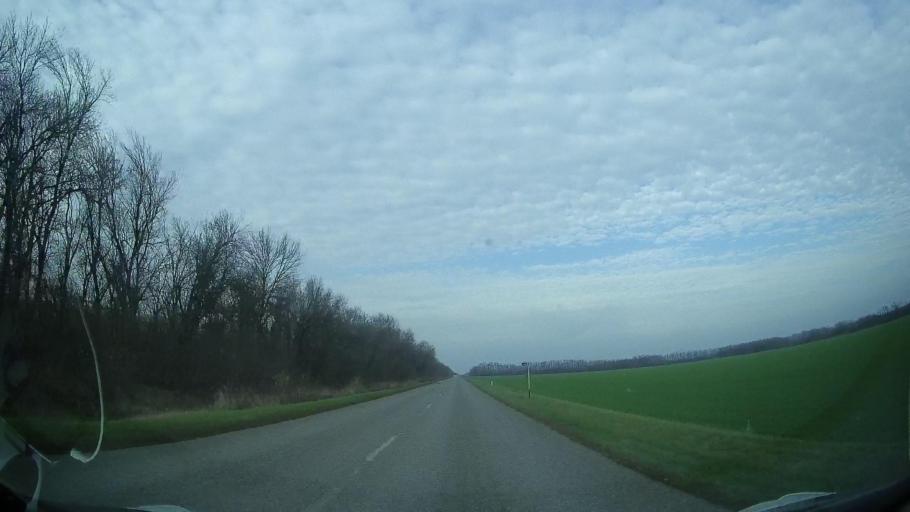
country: RU
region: Rostov
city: Zernograd
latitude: 46.9810
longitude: 40.3916
